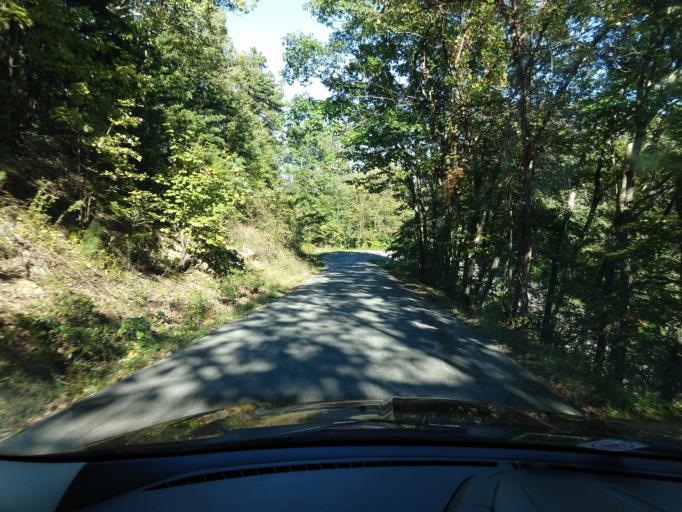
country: US
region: Virginia
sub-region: Alleghany County
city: Clifton Forge
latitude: 37.8706
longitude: -79.8797
